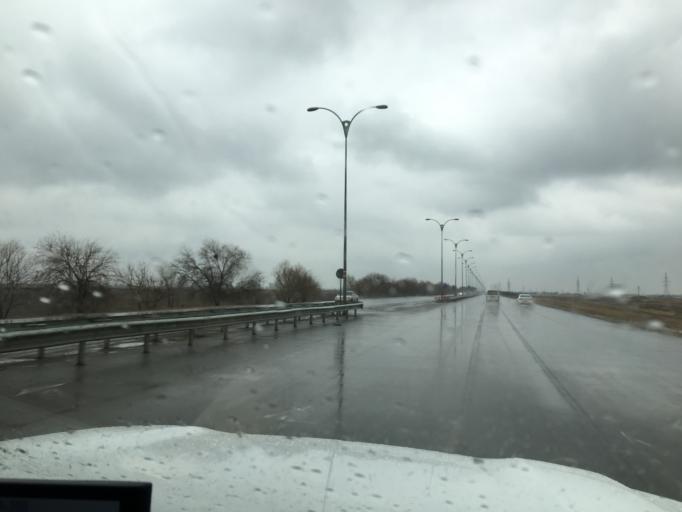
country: TM
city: Murgab
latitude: 37.5269
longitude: 61.9039
